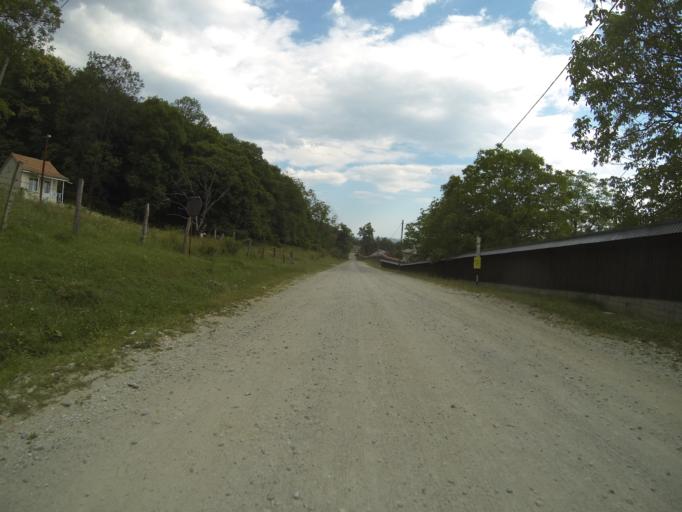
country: RO
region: Gorj
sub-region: Comuna Polovragi
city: Polovragi
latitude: 45.1941
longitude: 23.7897
